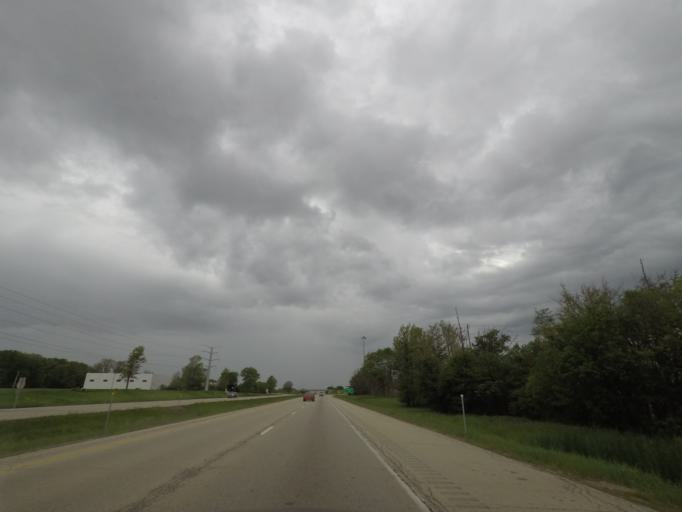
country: US
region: Illinois
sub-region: Winnebago County
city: Cherry Valley
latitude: 42.2202
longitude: -89.0210
